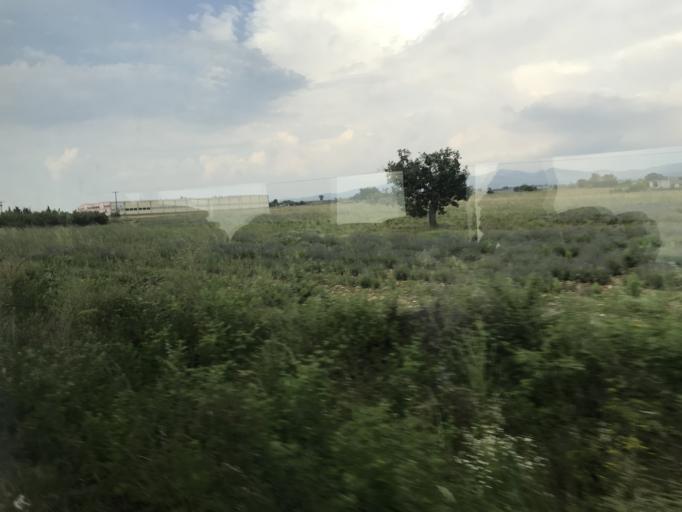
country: GR
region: East Macedonia and Thrace
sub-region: Nomos Rodopis
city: Sapes
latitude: 40.9719
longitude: 25.6436
